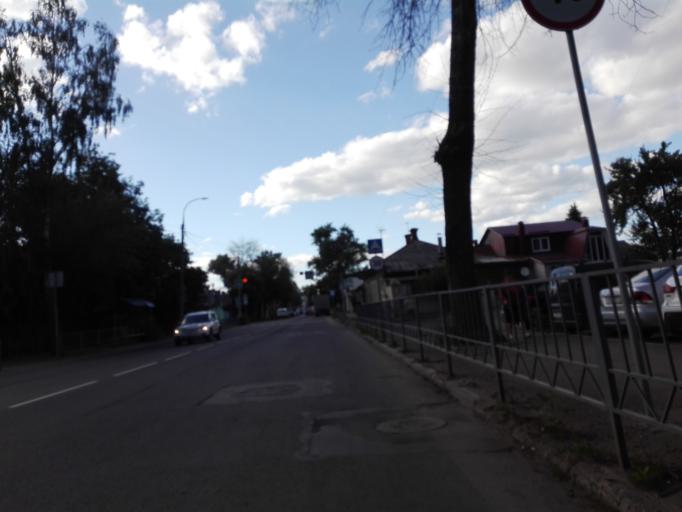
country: RU
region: Orjol
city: Orel
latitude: 52.9586
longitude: 36.0720
